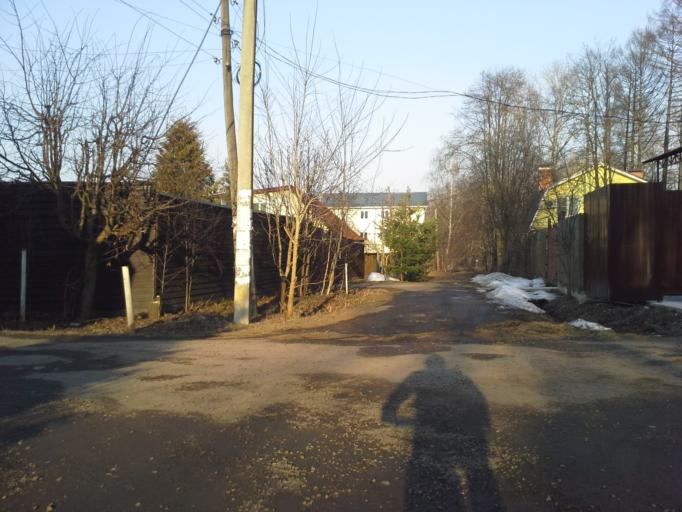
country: RU
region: Moscow
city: Novo-Peredelkino
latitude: 55.6470
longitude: 37.3134
